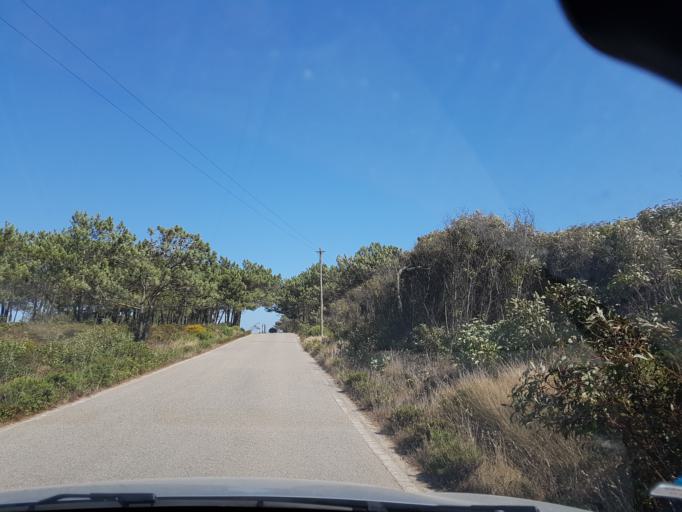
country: PT
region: Faro
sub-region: Vila do Bispo
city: Vila do Bispo
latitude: 37.0916
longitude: -8.9319
